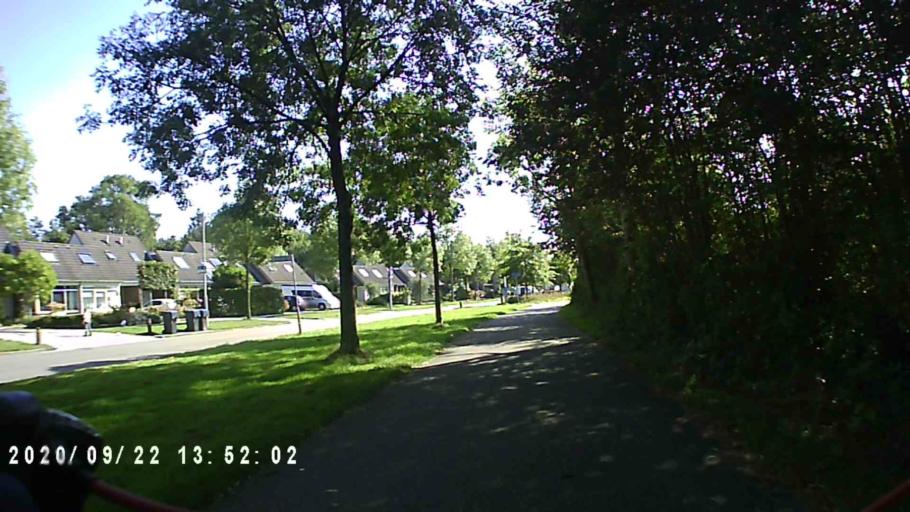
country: NL
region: Groningen
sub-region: Gemeente Leek
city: Leek
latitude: 53.1330
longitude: 6.4133
